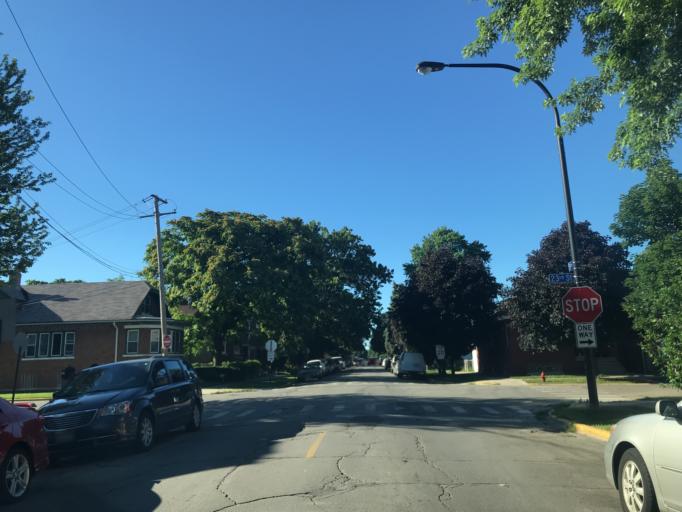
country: US
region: Illinois
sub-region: Cook County
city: Cicero
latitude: 41.8486
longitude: -87.7688
